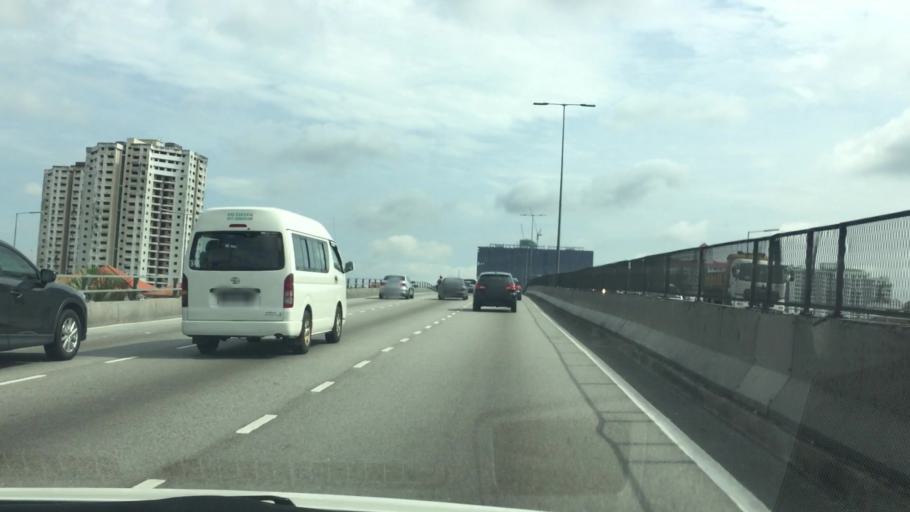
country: MY
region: Kuala Lumpur
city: Kuala Lumpur
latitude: 3.1451
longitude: 101.7439
